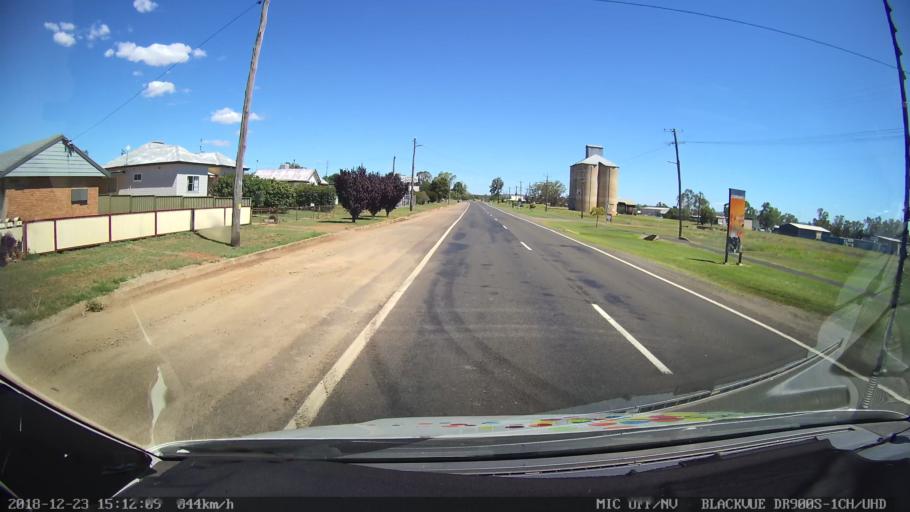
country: AU
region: New South Wales
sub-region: Tamworth Municipality
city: Manilla
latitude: -30.7534
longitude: 150.7271
